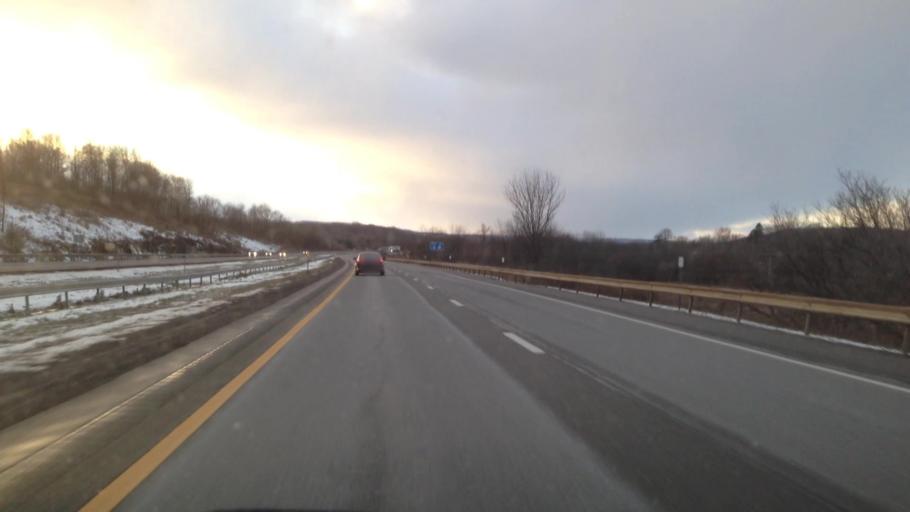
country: US
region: New York
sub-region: Herkimer County
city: Herkimer
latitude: 43.0143
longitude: -74.9655
